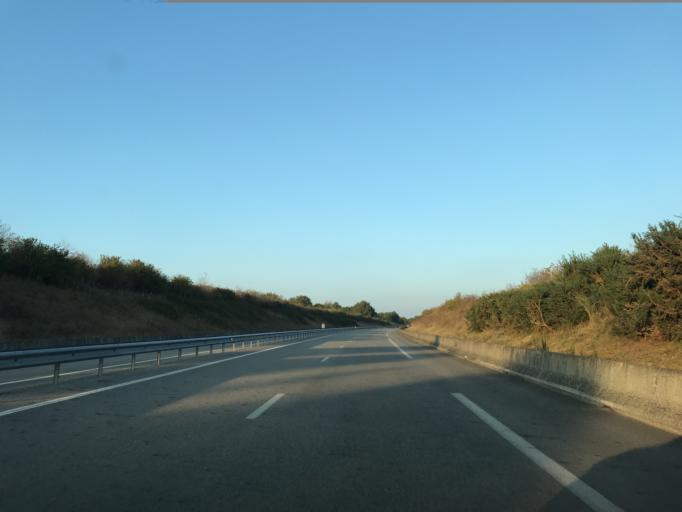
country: FR
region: Lower Normandy
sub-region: Departement de l'Orne
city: Sees
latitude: 48.4953
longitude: 0.2982
